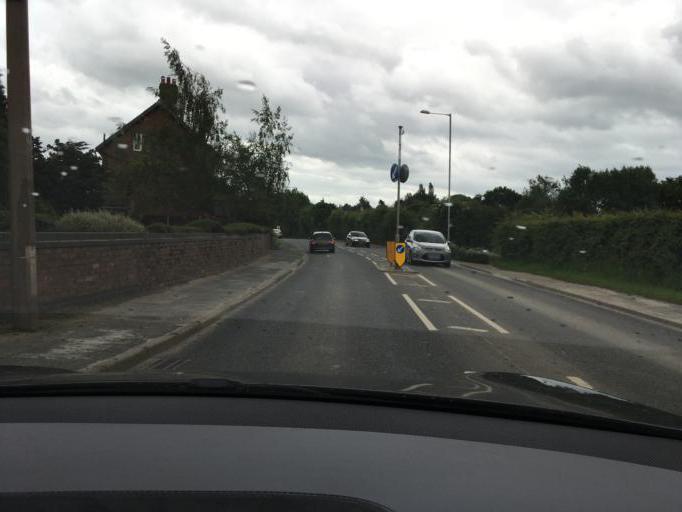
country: GB
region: England
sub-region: Borough of Stockport
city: Bramhall
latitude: 53.3479
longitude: -2.1612
